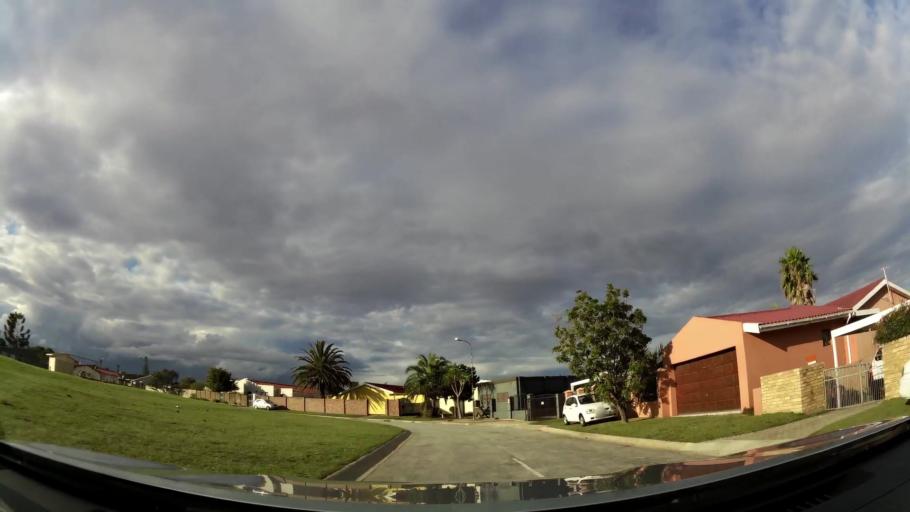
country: ZA
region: Eastern Cape
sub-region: Nelson Mandela Bay Metropolitan Municipality
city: Port Elizabeth
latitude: -33.9475
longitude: 25.4820
